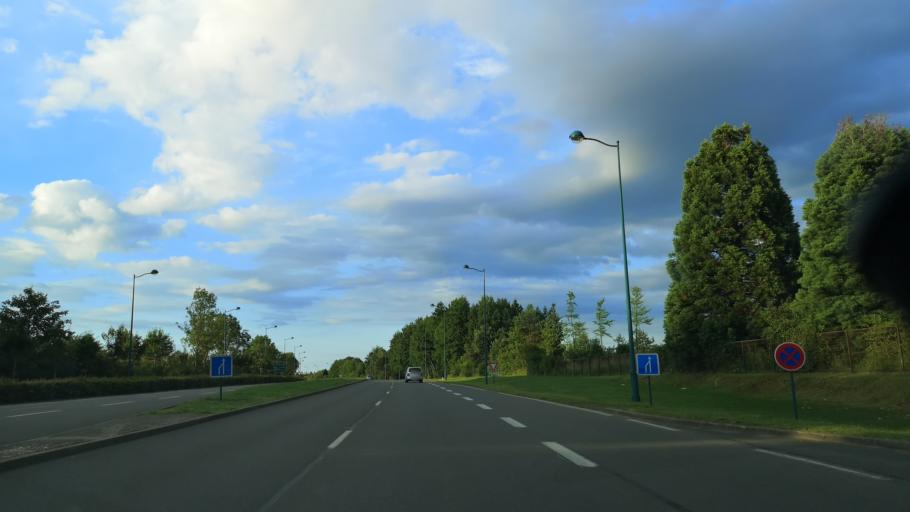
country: FR
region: Ile-de-France
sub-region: Departement de Seine-et-Marne
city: Magny-le-Hongre
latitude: 48.8558
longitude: 2.8024
